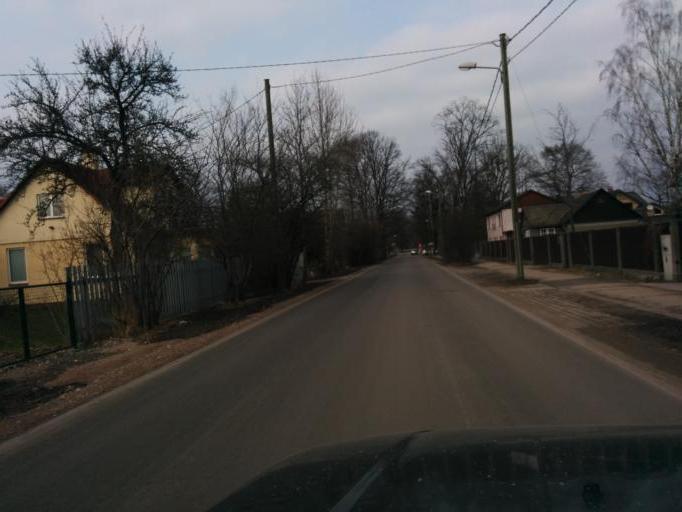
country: LV
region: Jurmala
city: Jurmala
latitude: 56.9575
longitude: 23.7233
